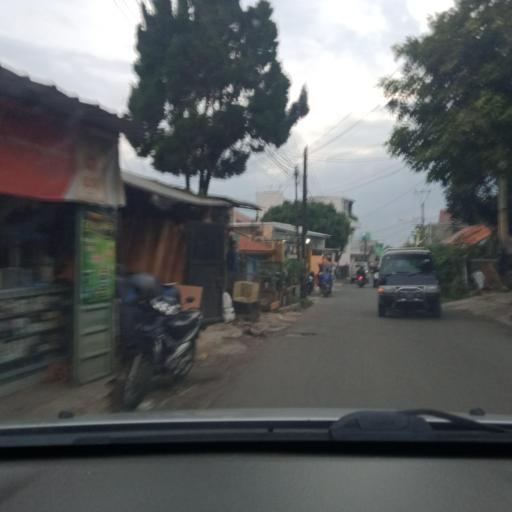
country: ID
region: West Java
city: Lembang
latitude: -6.8455
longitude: 107.5845
